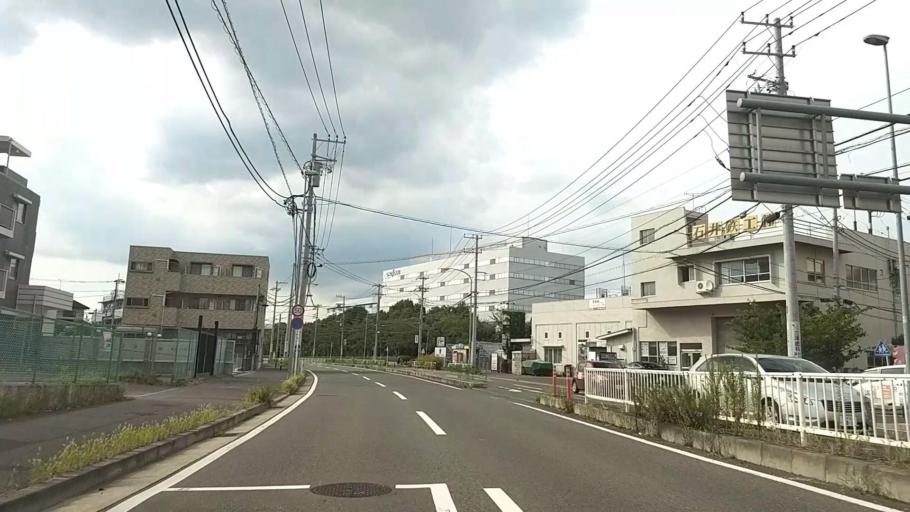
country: JP
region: Kanagawa
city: Yokohama
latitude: 35.5067
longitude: 139.5574
